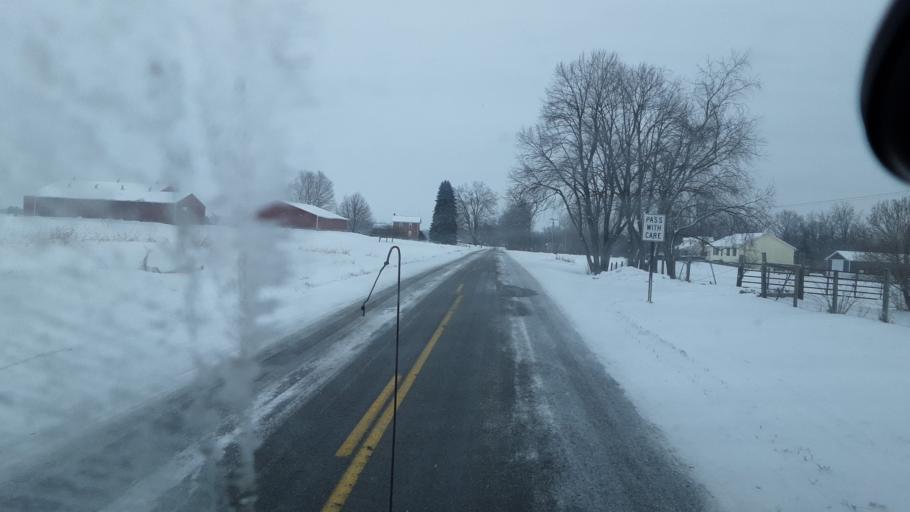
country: US
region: Michigan
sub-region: Ingham County
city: Leslie
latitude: 42.4308
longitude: -84.3168
